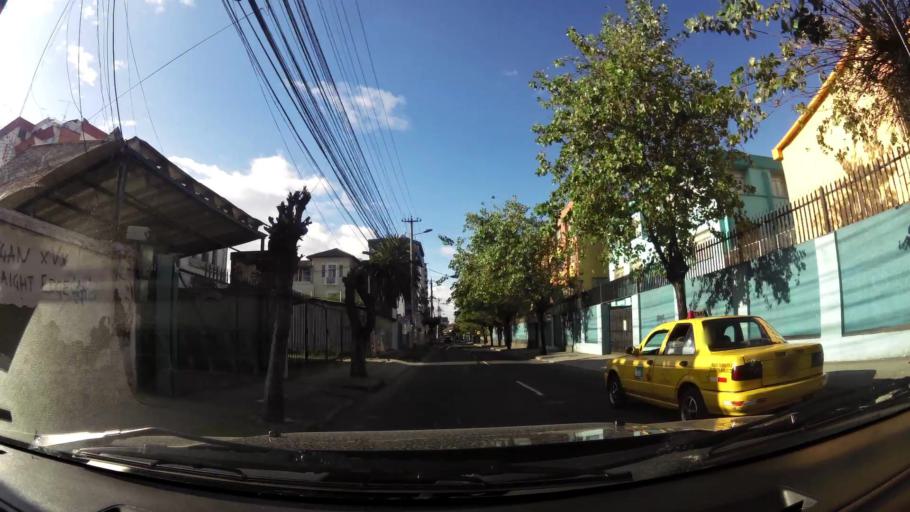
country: EC
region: Pichincha
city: Quito
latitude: -0.2012
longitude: -78.4947
